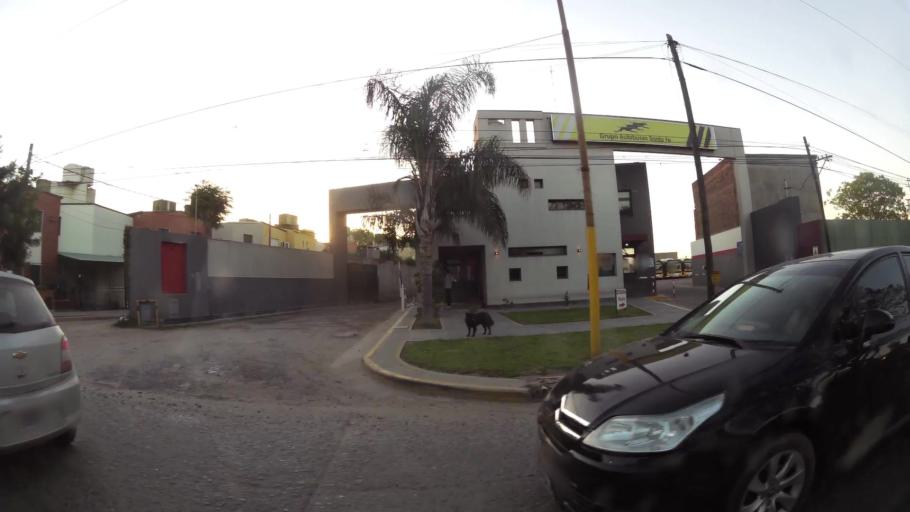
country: AR
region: Santa Fe
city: Santa Fe de la Vera Cruz
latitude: -31.5920
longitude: -60.6922
